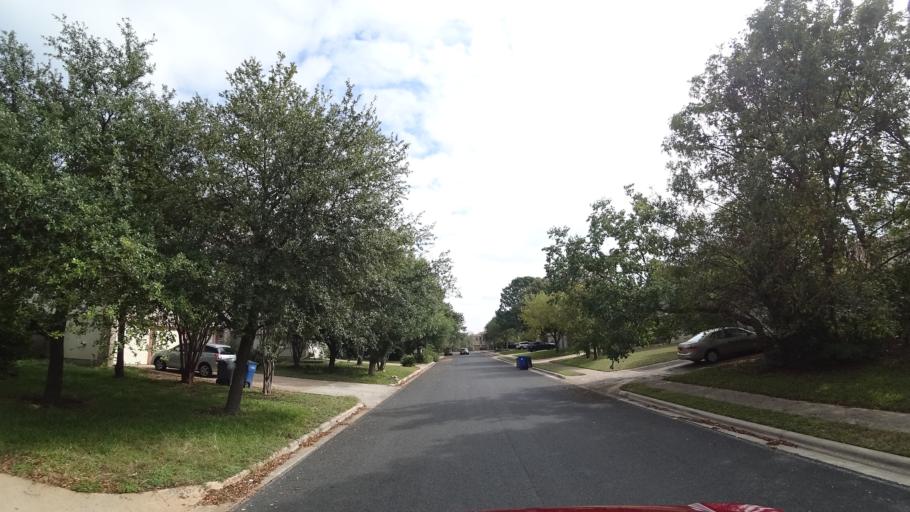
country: US
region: Texas
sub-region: Travis County
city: Wells Branch
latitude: 30.4238
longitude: -97.6953
